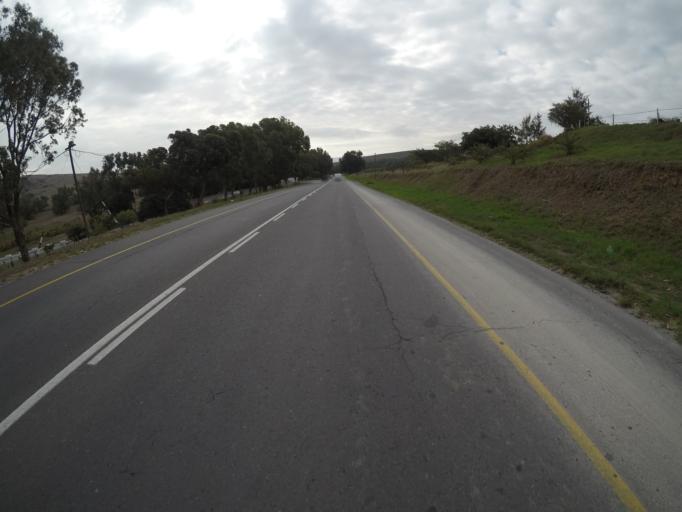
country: ZA
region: Western Cape
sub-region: City of Cape Town
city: Sunset Beach
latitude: -33.8234
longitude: 18.5793
